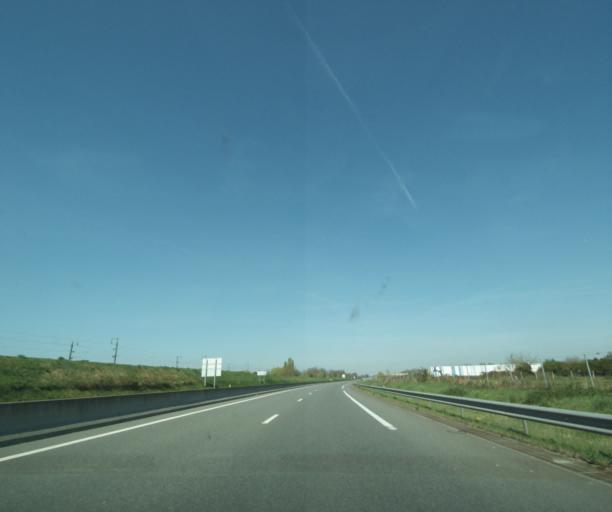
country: FR
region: Auvergne
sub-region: Departement de l'Allier
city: Avermes
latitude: 46.6047
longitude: 3.2986
